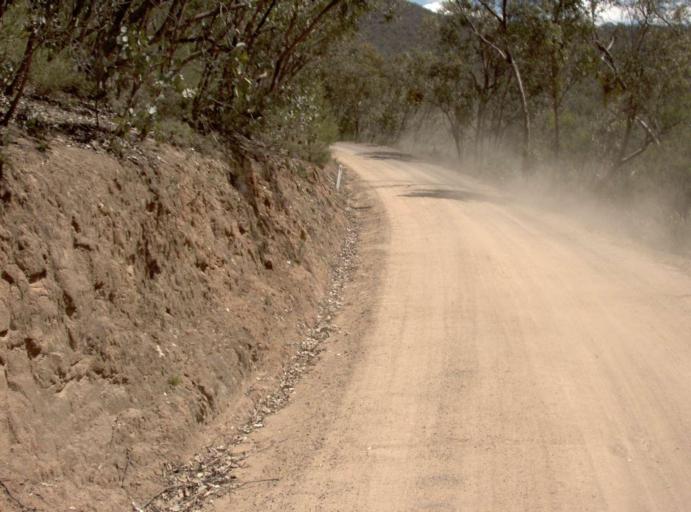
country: AU
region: New South Wales
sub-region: Snowy River
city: Jindabyne
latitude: -37.0626
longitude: 148.5175
